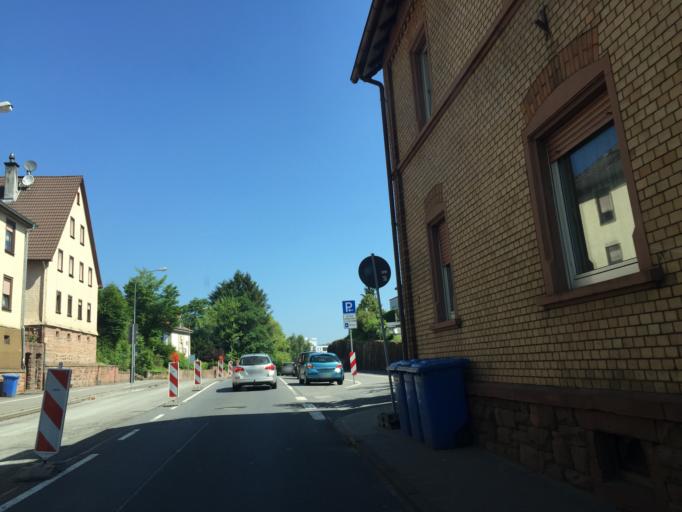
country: DE
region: Hesse
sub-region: Regierungsbezirk Darmstadt
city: Erbach
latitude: 49.6642
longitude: 8.9950
